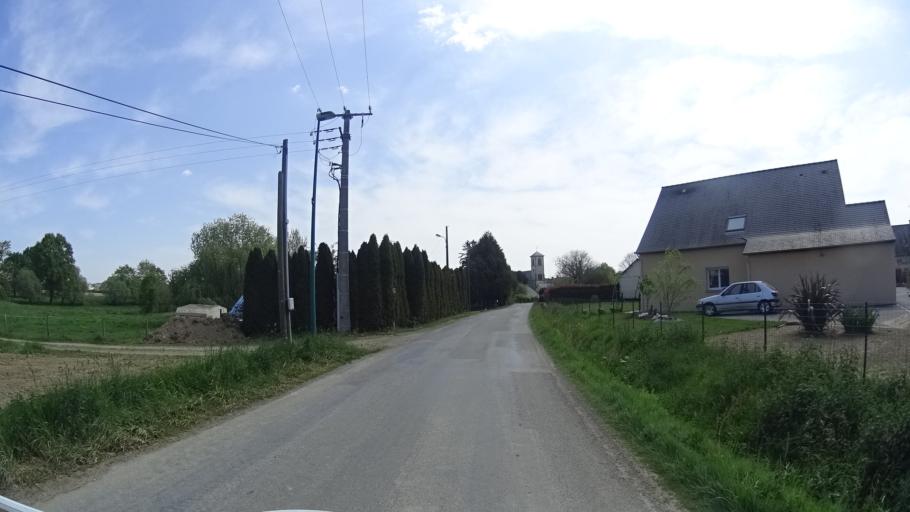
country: FR
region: Brittany
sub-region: Departement d'Ille-et-Vilaine
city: Torce
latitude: 48.0373
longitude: -1.2697
